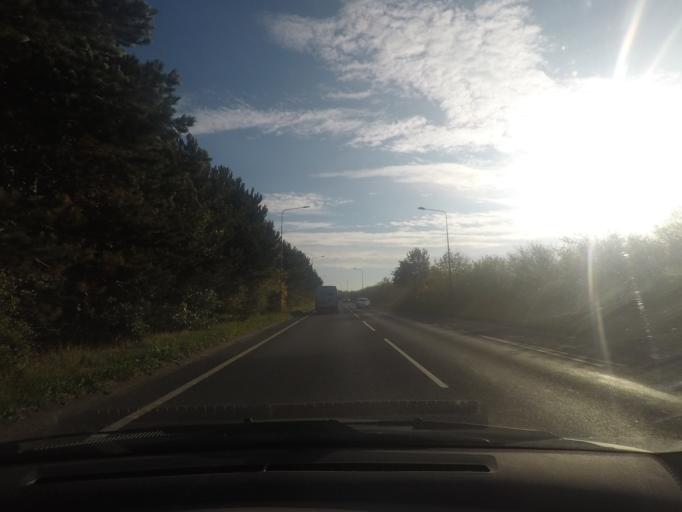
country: GB
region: England
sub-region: East Riding of Yorkshire
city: Market Weighton
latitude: 53.8573
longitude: -0.6676
